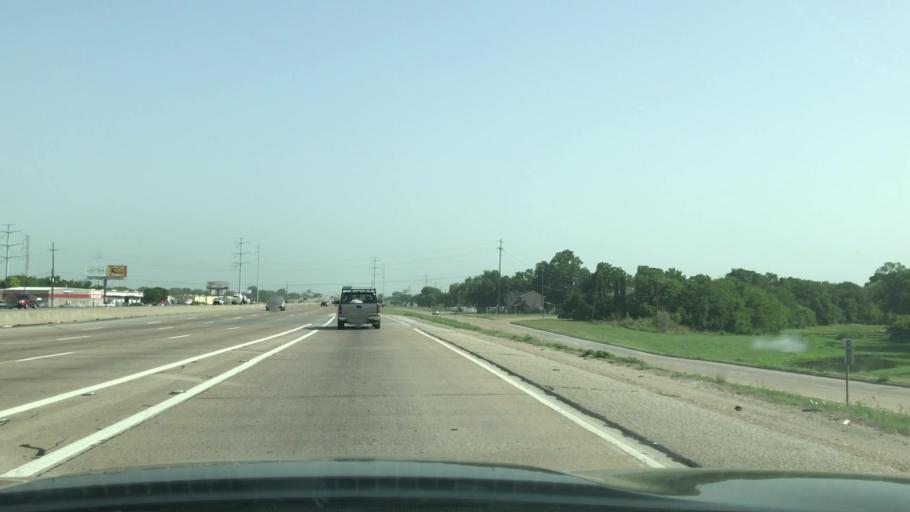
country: US
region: Texas
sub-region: Dallas County
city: Cockrell Hill
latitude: 32.7706
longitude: -96.9151
